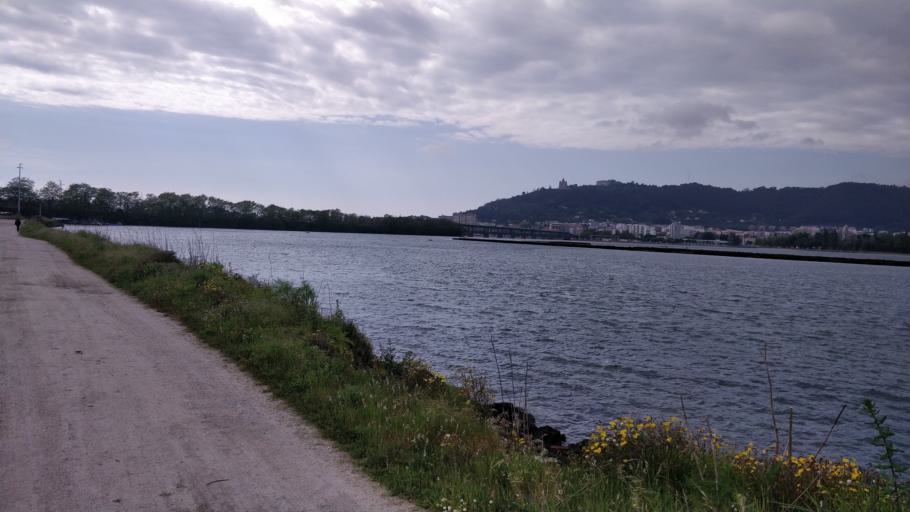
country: PT
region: Viana do Castelo
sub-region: Viana do Castelo
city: Meadela
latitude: 41.6881
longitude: -8.8072
